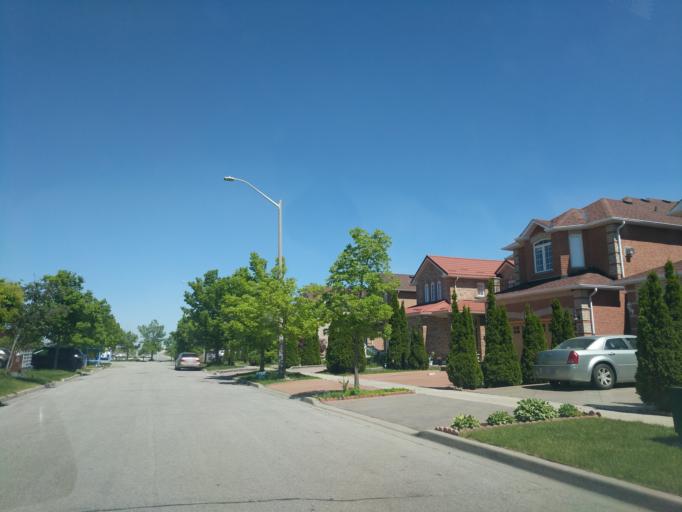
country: CA
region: Ontario
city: Markham
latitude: 43.8504
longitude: -79.2690
